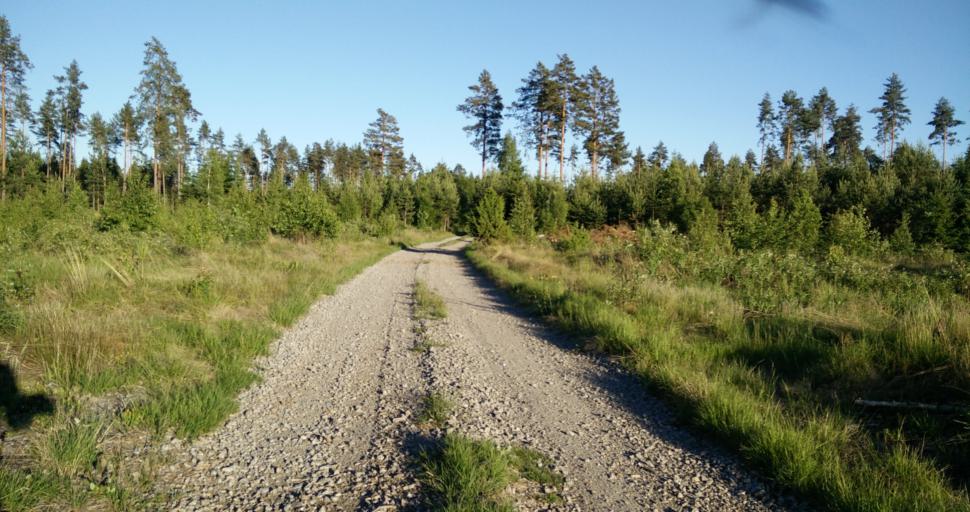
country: SE
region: Vaermland
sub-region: Hagfors Kommun
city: Hagfors
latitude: 60.0226
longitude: 13.5884
